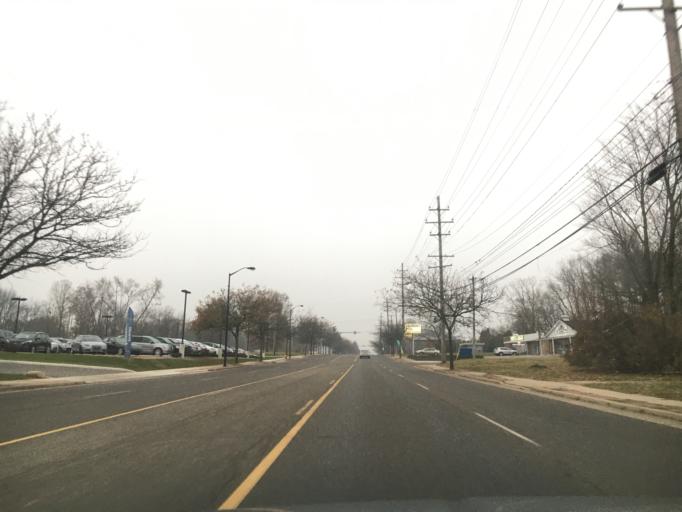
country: US
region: Ohio
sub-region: Summit County
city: Cuyahoga Falls
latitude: 41.1156
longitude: -81.4855
